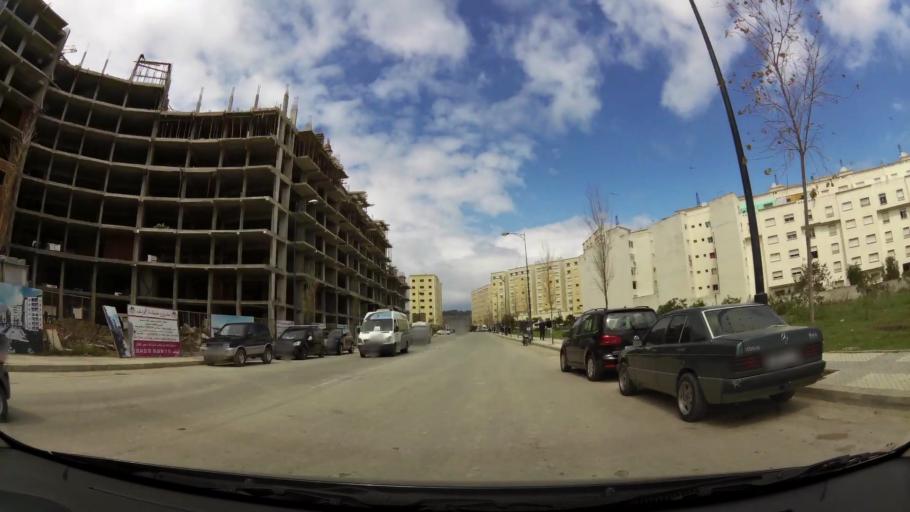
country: MA
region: Tanger-Tetouan
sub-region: Tanger-Assilah
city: Boukhalef
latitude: 35.7642
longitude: -5.8565
